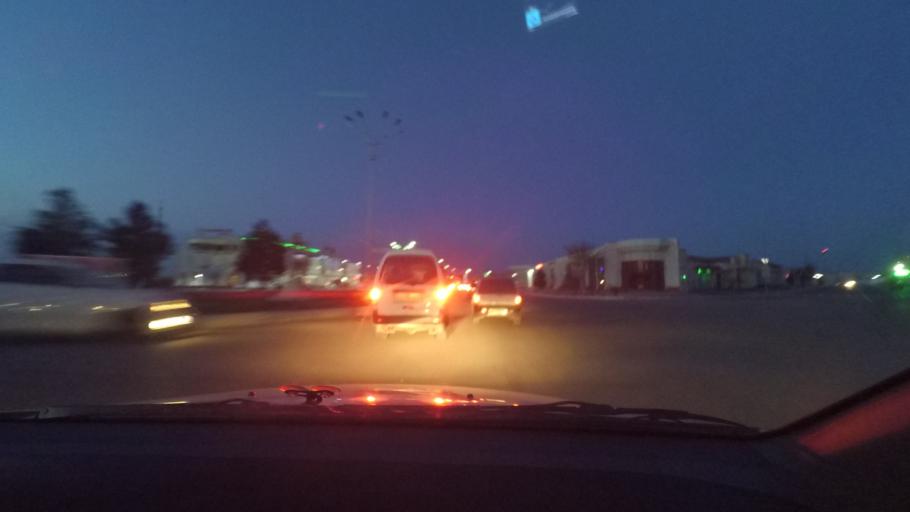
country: UZ
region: Bukhara
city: Bukhara
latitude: 39.7817
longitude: 64.4120
